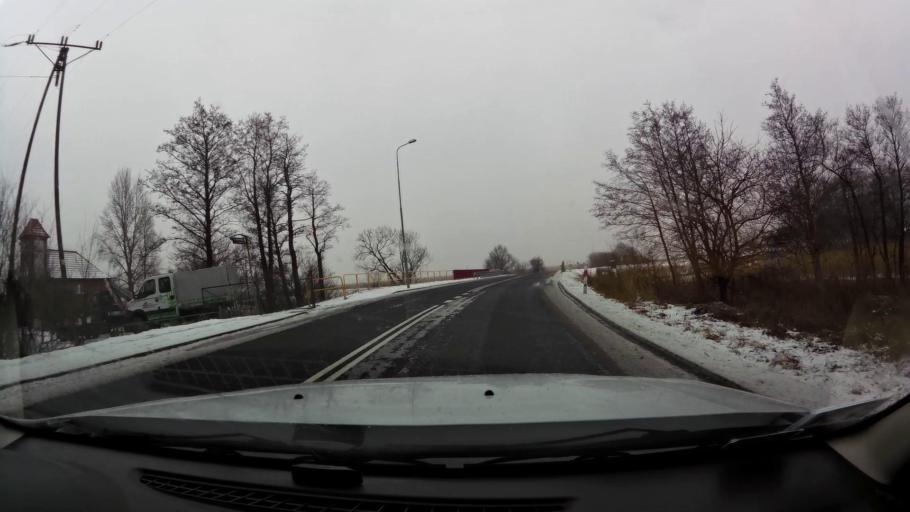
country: PL
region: West Pomeranian Voivodeship
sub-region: Powiat gryficki
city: Mrzezyno
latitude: 54.1346
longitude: 15.2838
